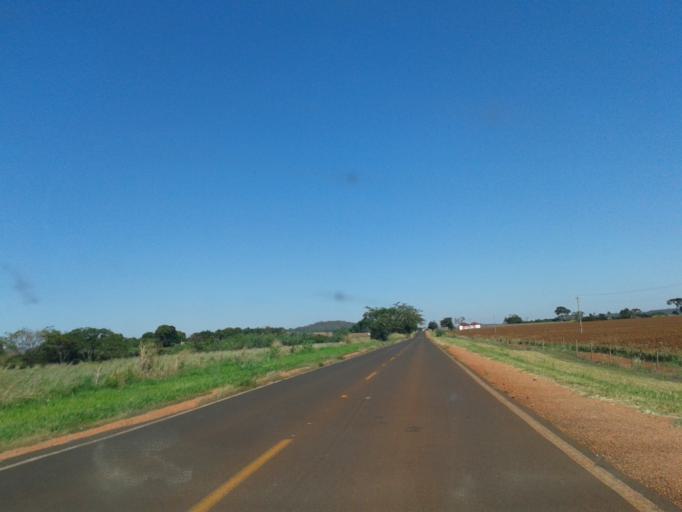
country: BR
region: Minas Gerais
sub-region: Capinopolis
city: Capinopolis
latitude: -18.5850
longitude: -49.5133
